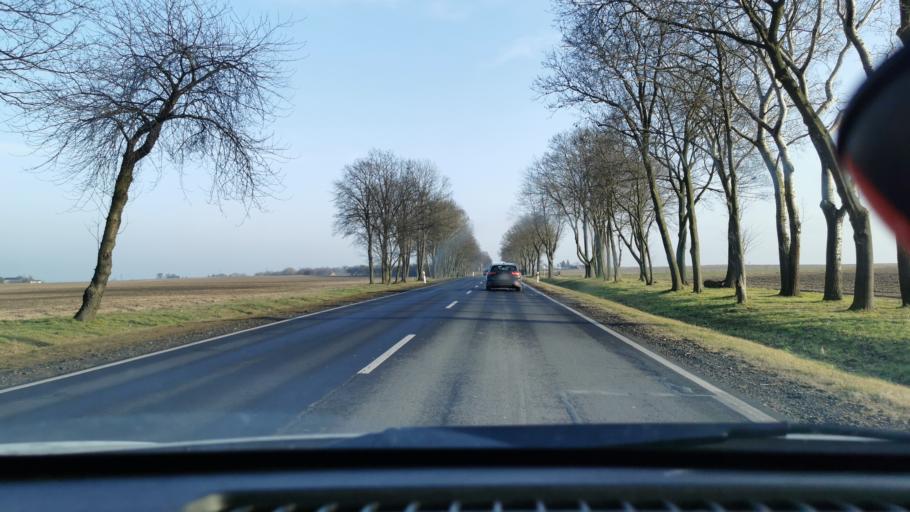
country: PL
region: Lodz Voivodeship
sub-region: Powiat sieradzki
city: Wroblew
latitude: 51.6198
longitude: 18.5879
